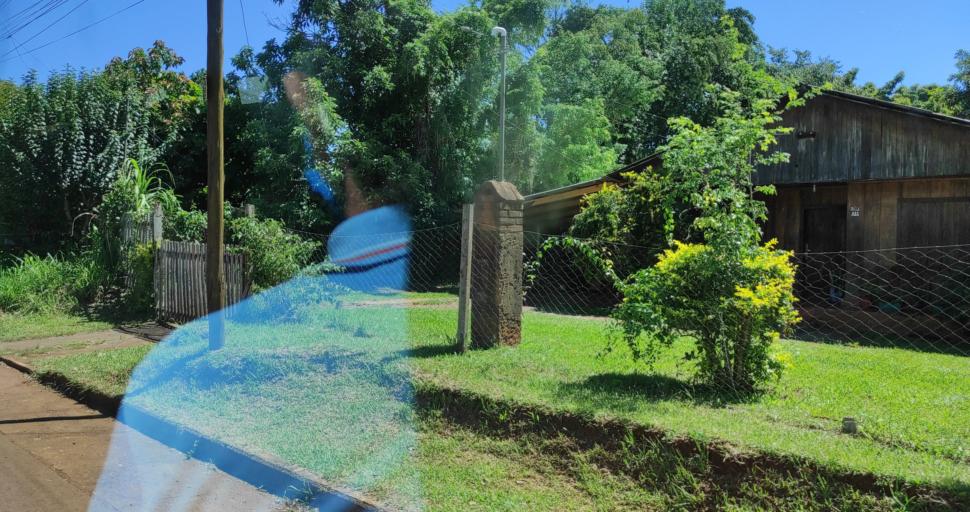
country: AR
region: Misiones
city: El Soberbio
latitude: -27.2998
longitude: -54.1940
